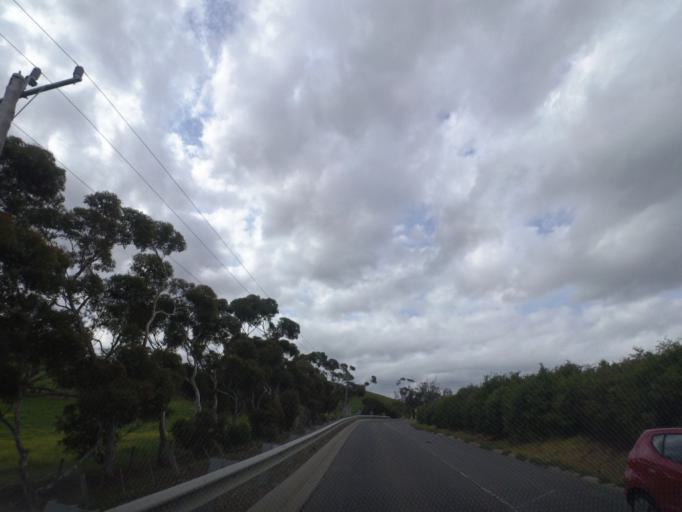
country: AU
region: Victoria
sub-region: Brimbank
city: Keilor
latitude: -37.7007
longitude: 144.8356
